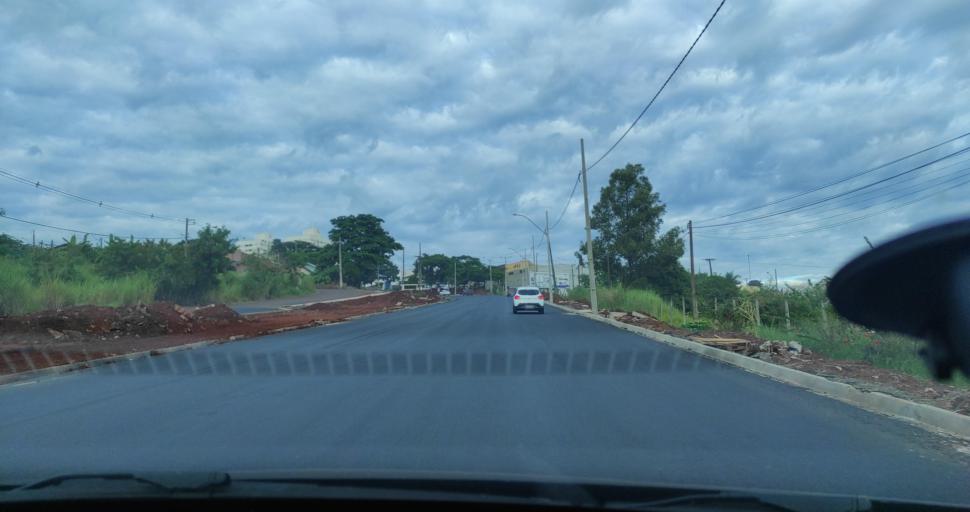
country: BR
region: Parana
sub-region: Ibipora
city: Ibipora
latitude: -23.2512
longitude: -51.0486
